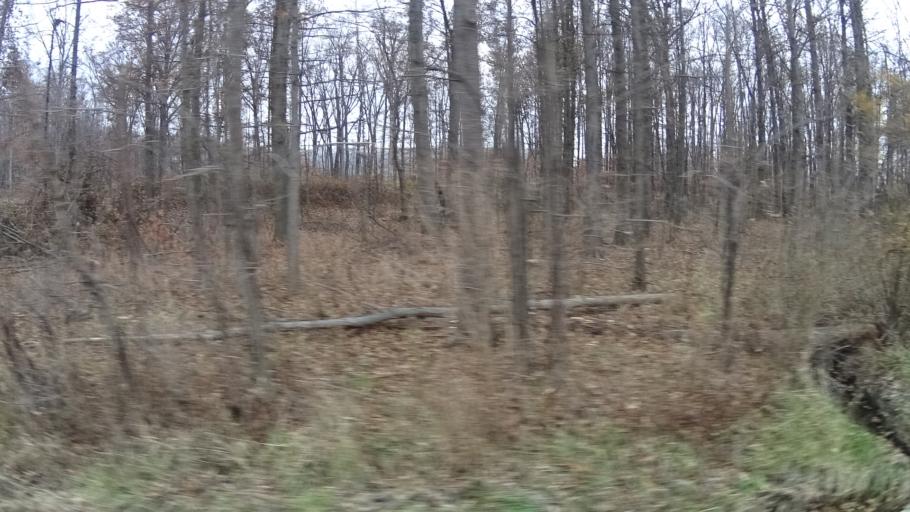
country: US
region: Ohio
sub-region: Cuyahoga County
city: Strongsville
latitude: 41.3014
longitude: -81.8778
